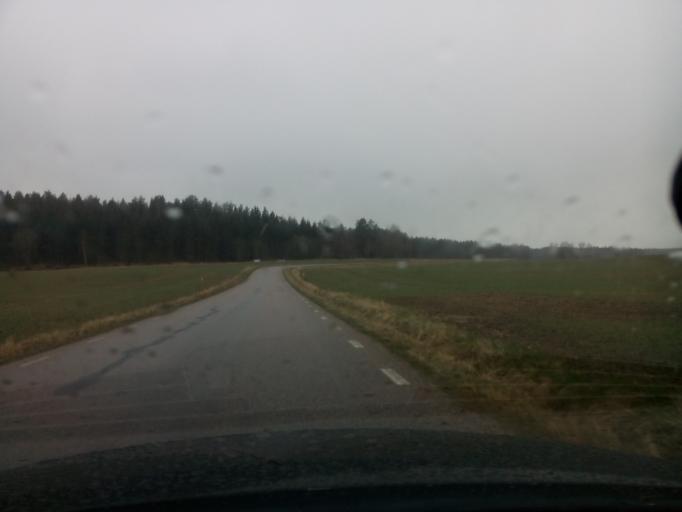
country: SE
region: Soedermanland
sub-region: Nykopings Kommun
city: Stigtomta
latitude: 58.9020
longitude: 16.7844
